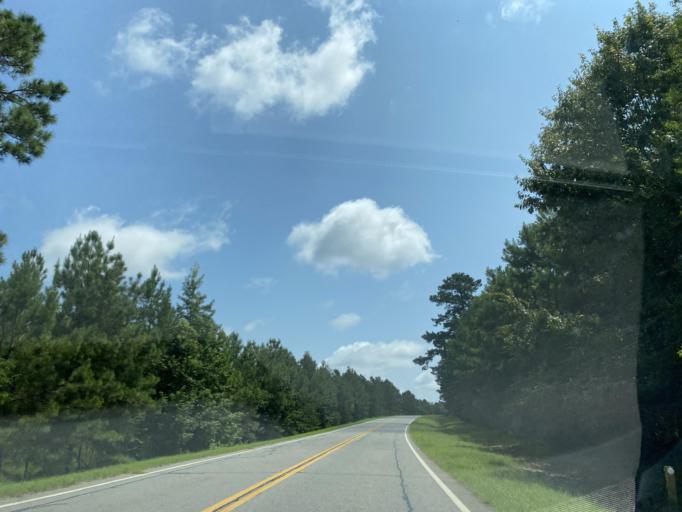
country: US
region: Georgia
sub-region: Wilcox County
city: Abbeville
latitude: 32.0052
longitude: -83.1667
